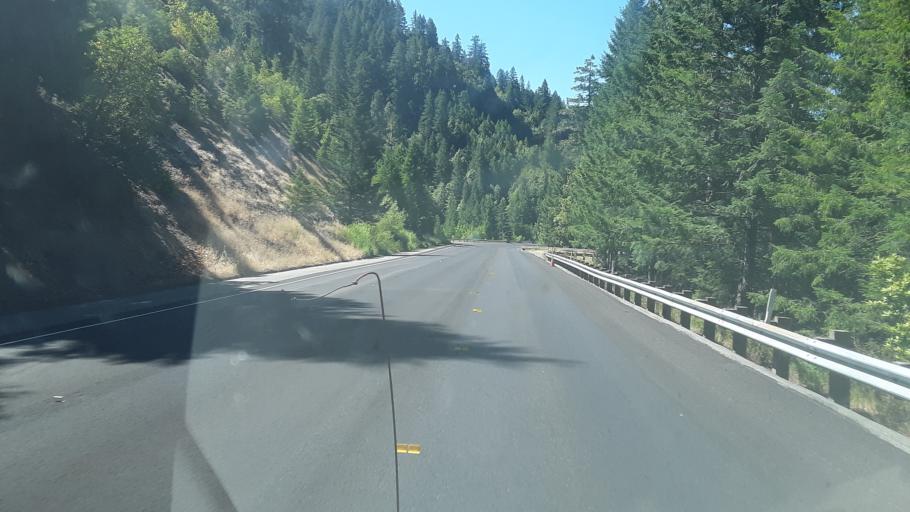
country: US
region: Oregon
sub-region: Josephine County
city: Cave Junction
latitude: 41.9534
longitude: -123.7432
